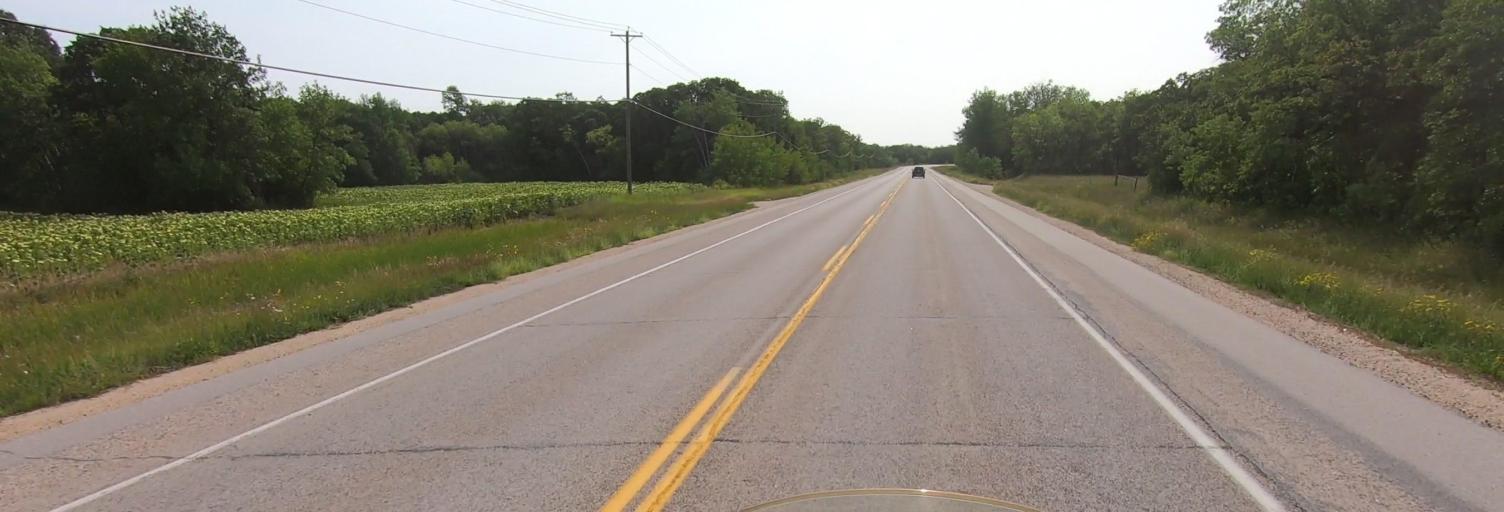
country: CA
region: Manitoba
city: Niverville
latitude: 49.7301
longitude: -97.0969
